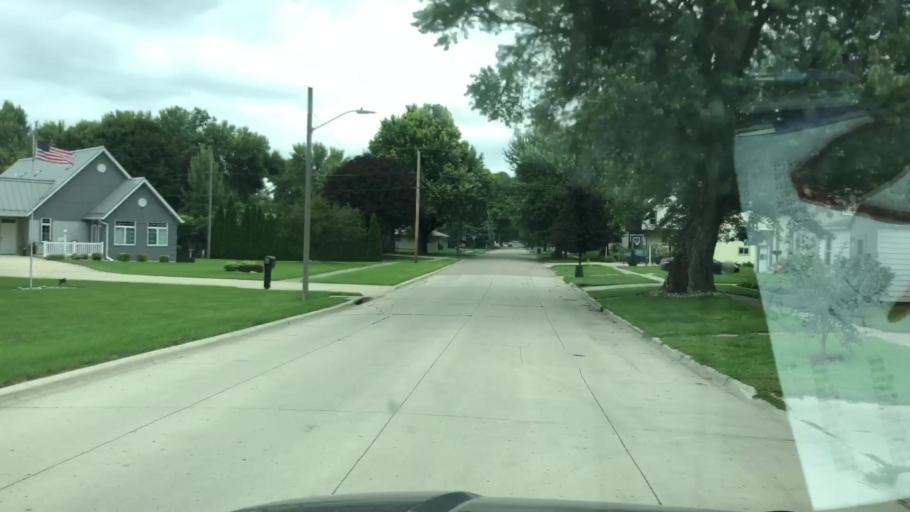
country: US
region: Iowa
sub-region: O'Brien County
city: Sheldon
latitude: 43.1754
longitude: -95.8490
